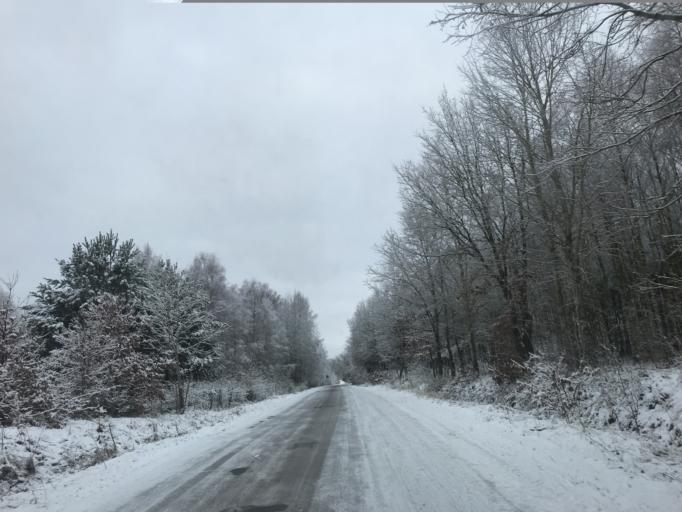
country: PL
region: Pomeranian Voivodeship
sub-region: Powiat bytowski
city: Parchowo
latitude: 54.2328
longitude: 17.5732
